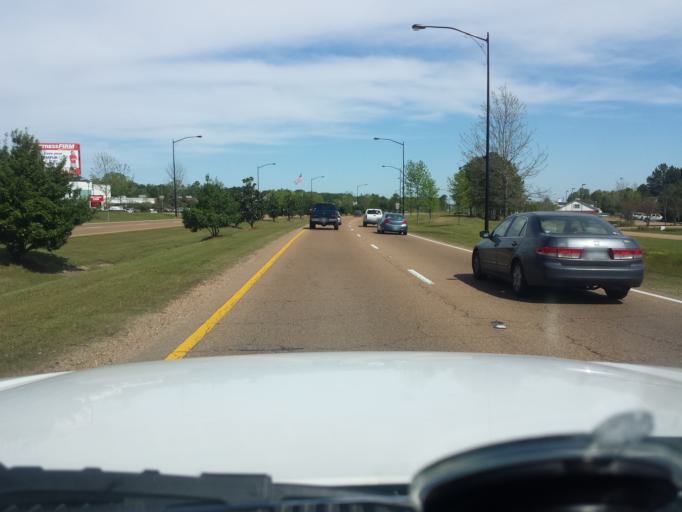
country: US
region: Mississippi
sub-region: Rankin County
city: Pearl
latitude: 32.2788
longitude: -90.0735
